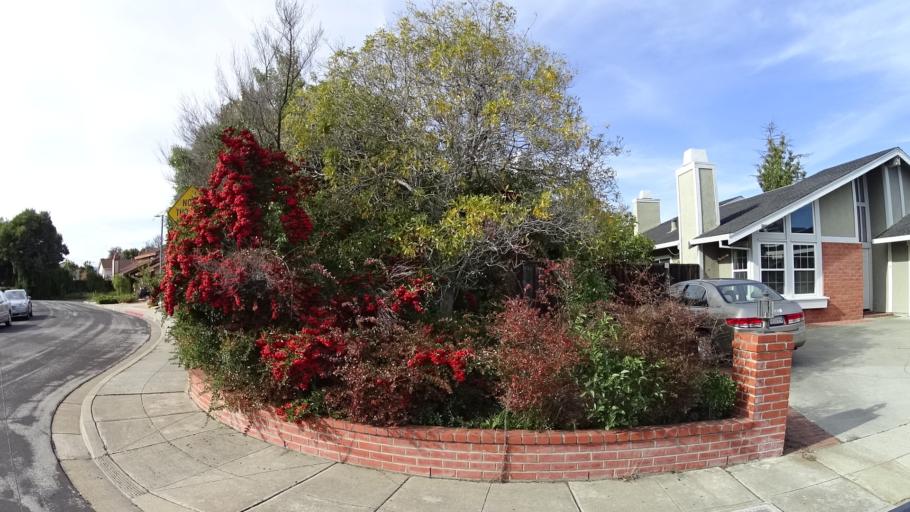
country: US
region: California
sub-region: San Mateo County
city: Foster City
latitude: 37.5409
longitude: -122.2706
